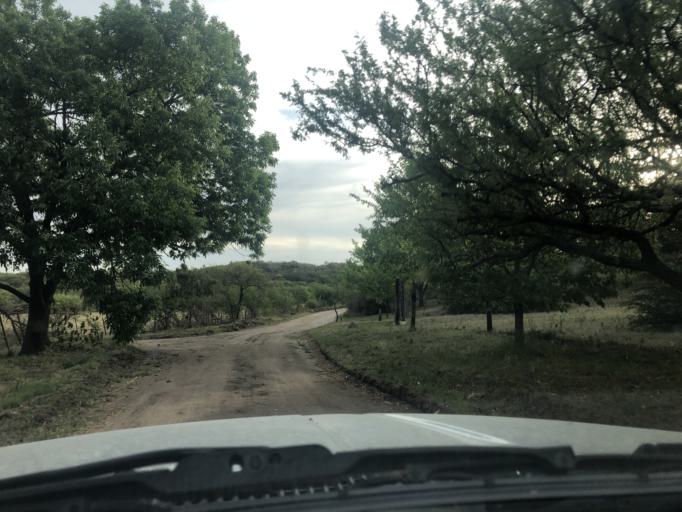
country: AR
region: Cordoba
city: La Granja
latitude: -31.0140
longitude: -64.2520
